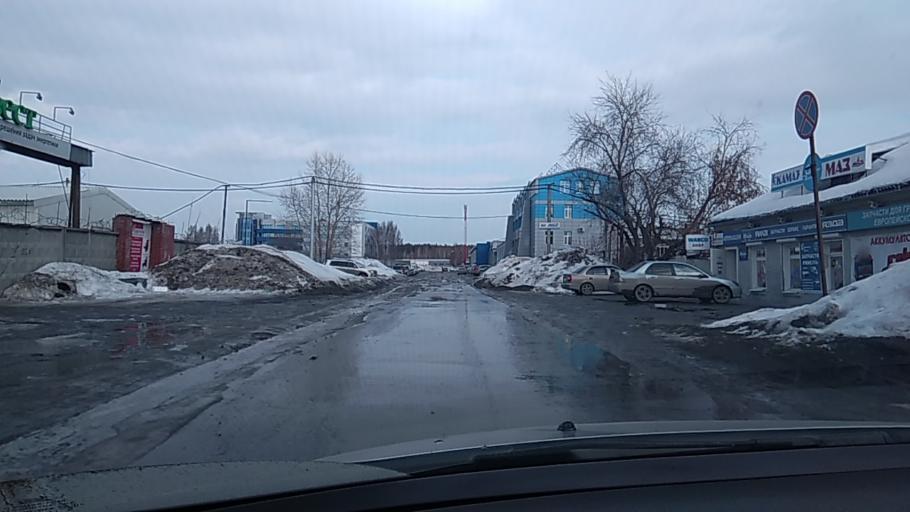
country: RU
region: Sverdlovsk
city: Yekaterinburg
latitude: 56.8621
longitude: 60.6673
